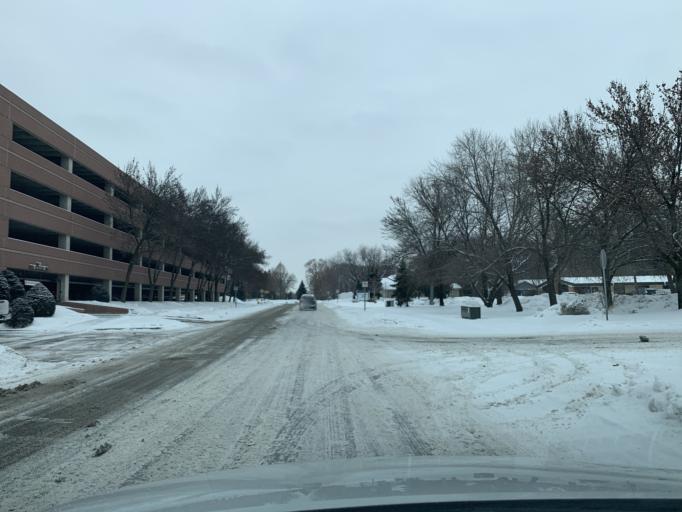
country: US
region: Minnesota
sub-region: Hennepin County
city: Saint Louis Park
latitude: 44.9716
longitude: -93.3495
